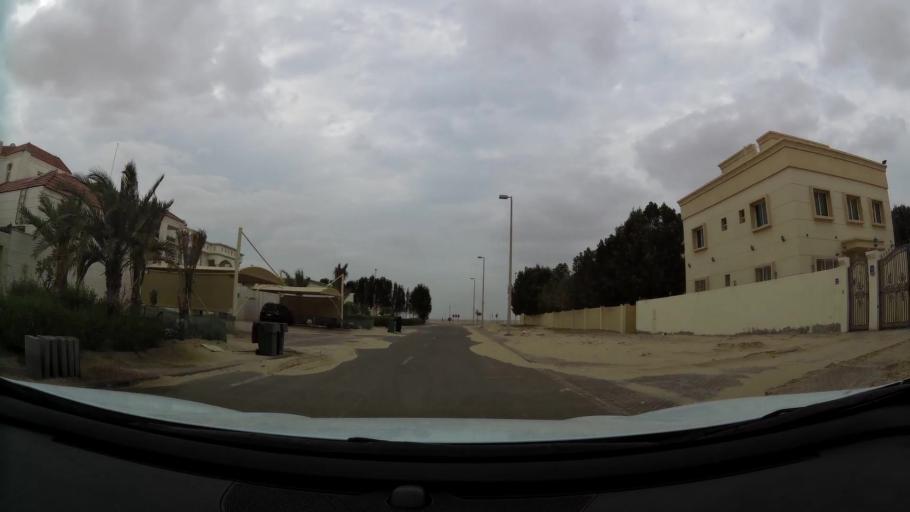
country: AE
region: Abu Dhabi
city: Abu Dhabi
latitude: 24.3781
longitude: 54.6326
